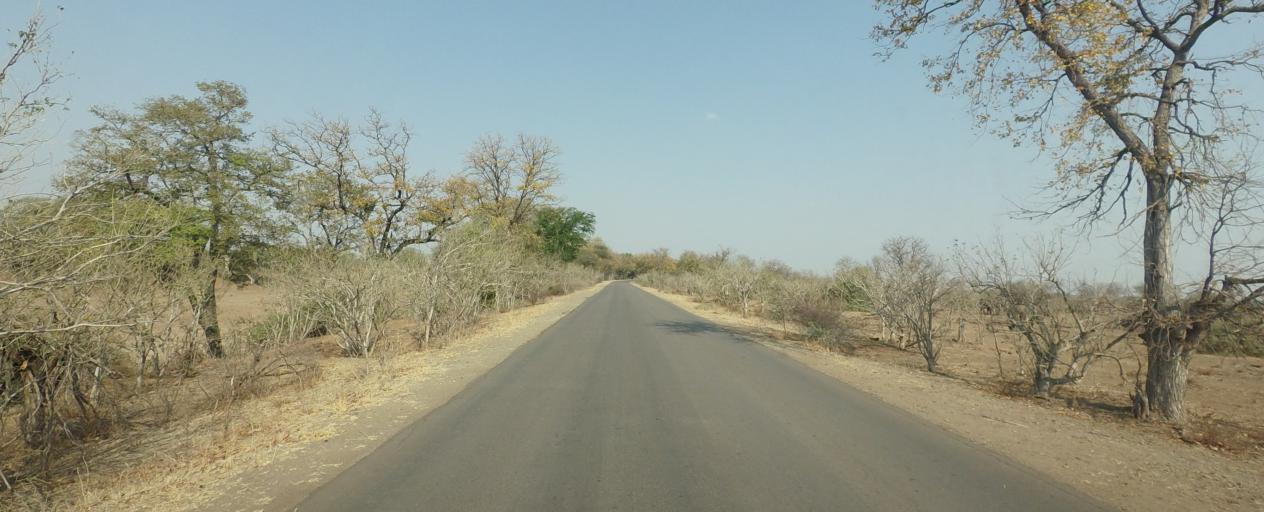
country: ZA
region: Limpopo
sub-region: Mopani District Municipality
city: Giyani
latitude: -23.0964
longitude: 31.4213
